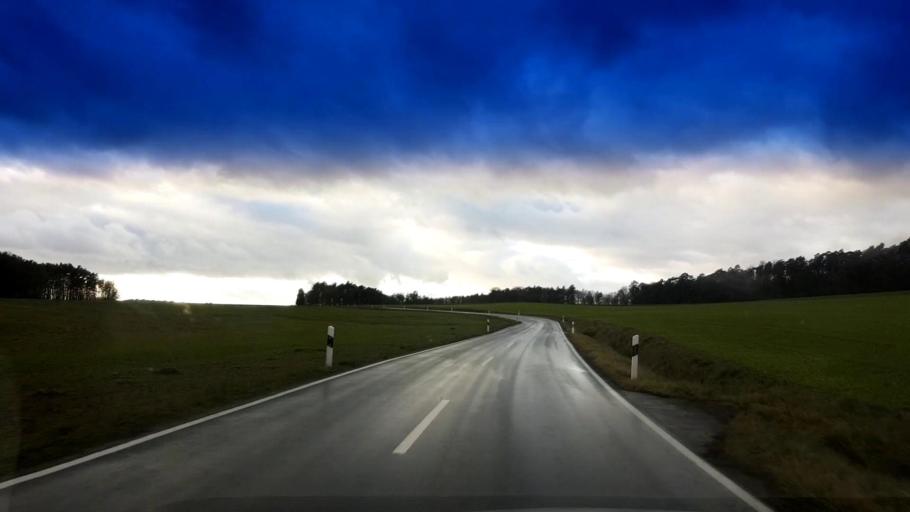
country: DE
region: Bavaria
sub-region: Upper Franconia
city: Lauter
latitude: 50.0024
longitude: 10.7687
